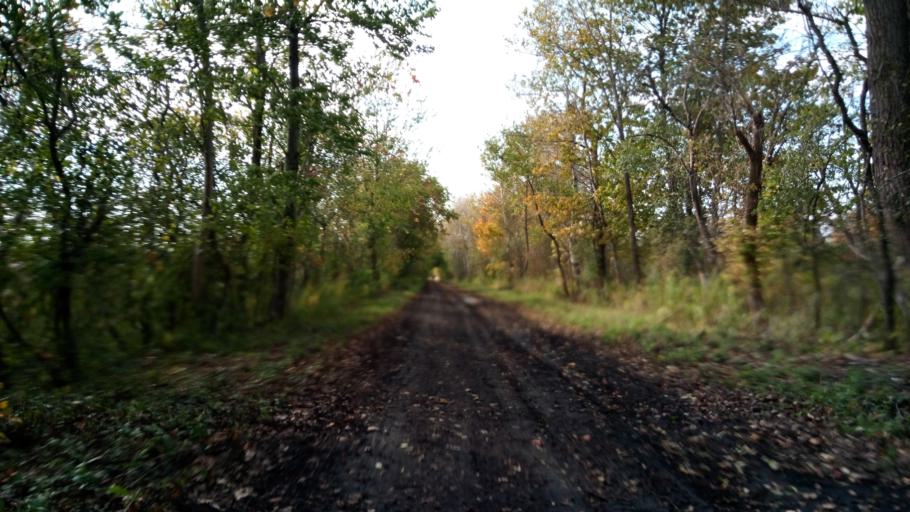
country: US
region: New York
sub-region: Wayne County
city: Clyde
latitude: 43.0655
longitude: -76.8342
